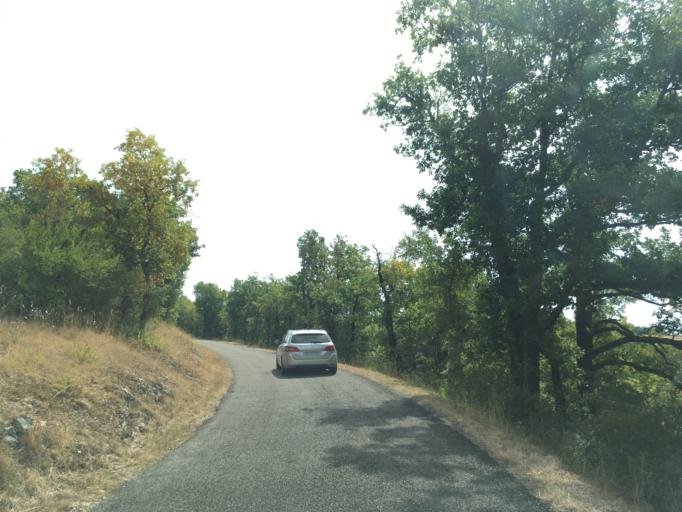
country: FR
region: Midi-Pyrenees
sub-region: Departement du Lot
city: Le Vigan
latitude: 44.7584
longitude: 1.5535
